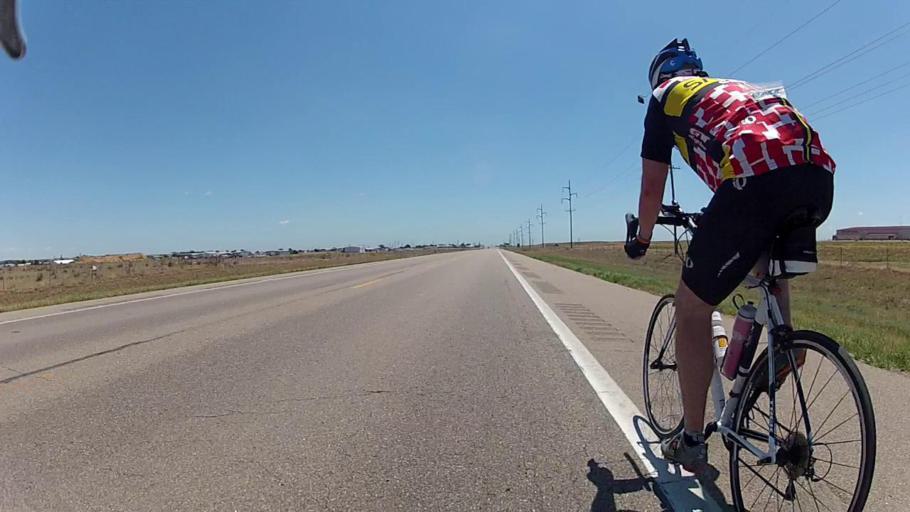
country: US
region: Kansas
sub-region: Ford County
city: Dodge City
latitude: 37.7218
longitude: -100.0233
